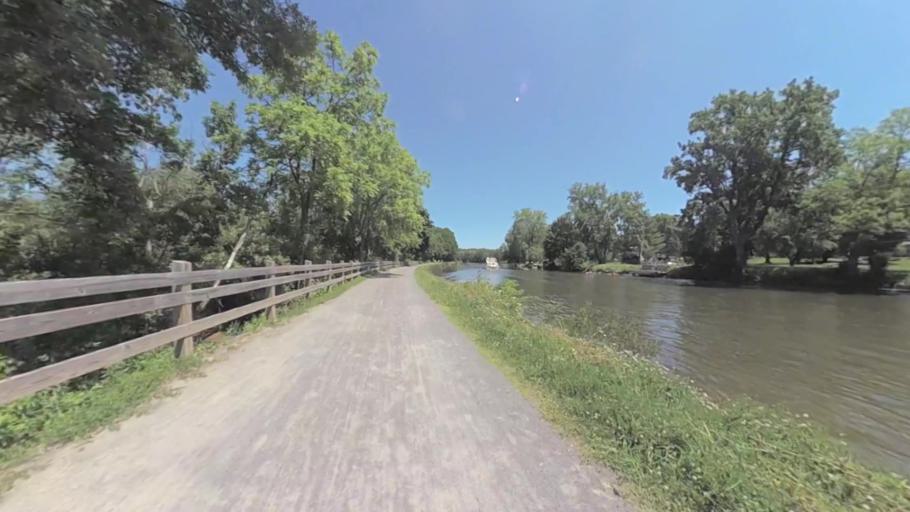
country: US
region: New York
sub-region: Monroe County
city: Fairport
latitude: 43.0845
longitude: -77.4591
